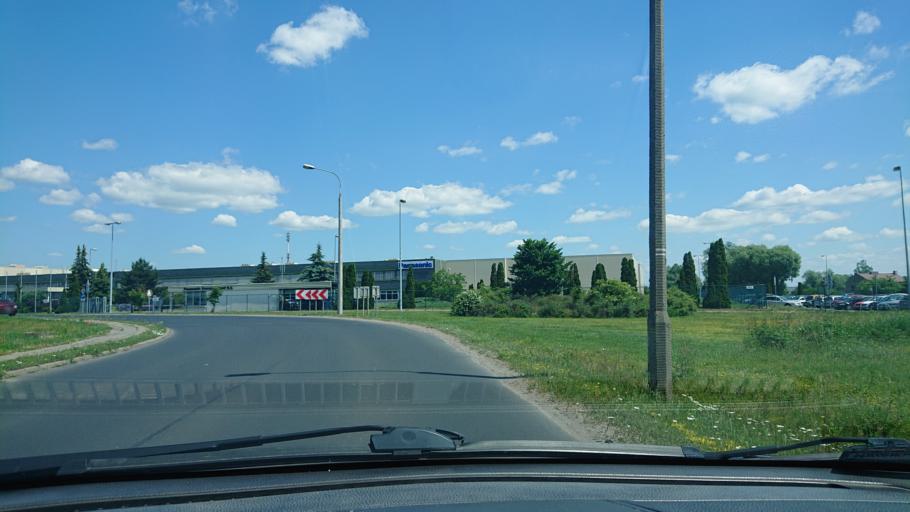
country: PL
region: Greater Poland Voivodeship
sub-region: Powiat gnieznienski
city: Gniezno
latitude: 52.5259
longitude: 17.6182
